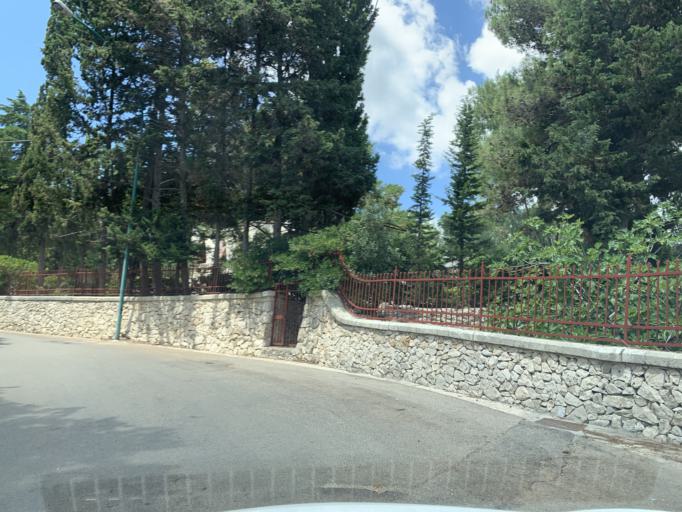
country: IT
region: Apulia
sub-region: Provincia di Lecce
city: Santa Cesarea Terme
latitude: 40.0335
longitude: 18.4466
